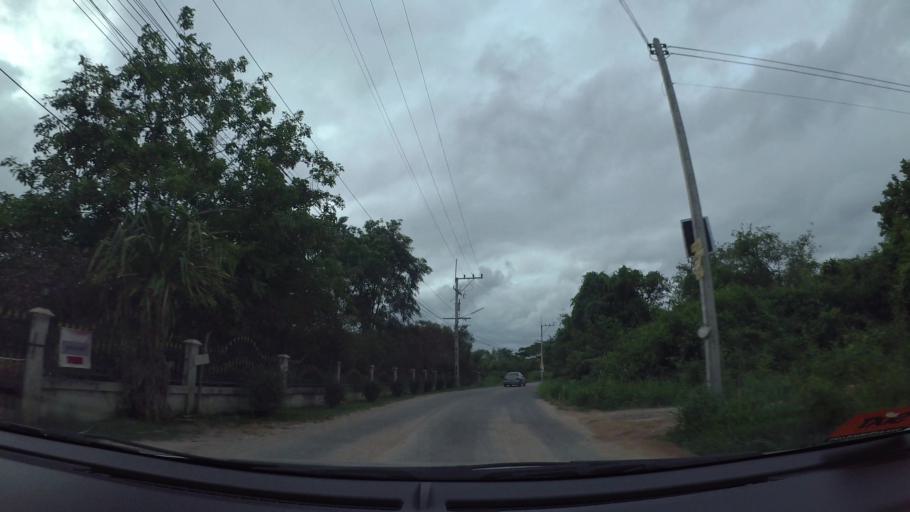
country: TH
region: Chon Buri
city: Sattahip
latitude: 12.6952
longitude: 100.9017
